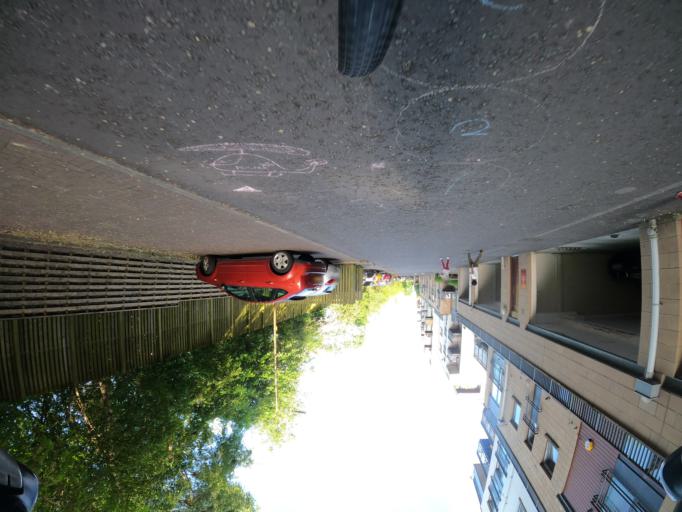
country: GB
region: Scotland
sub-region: Edinburgh
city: Edinburgh
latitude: 55.9712
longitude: -3.2281
